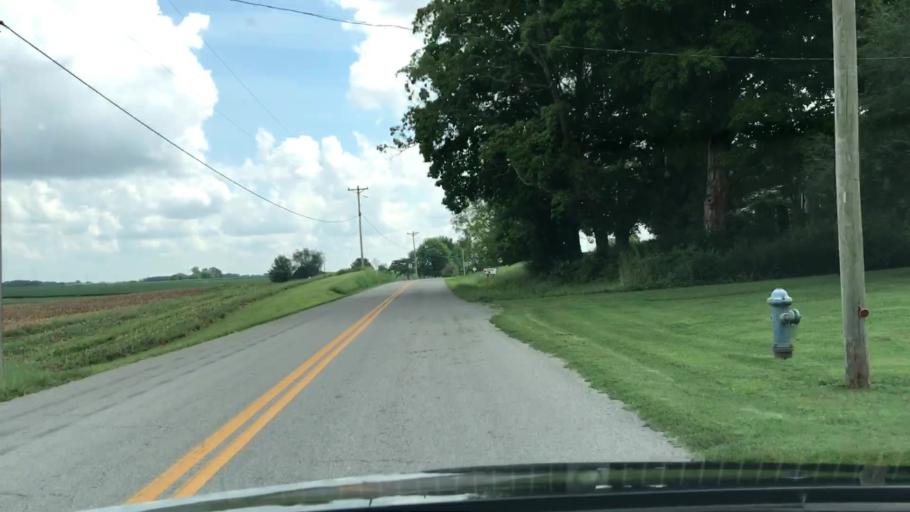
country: US
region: Kentucky
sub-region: Todd County
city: Guthrie
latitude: 36.7143
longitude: -87.0649
